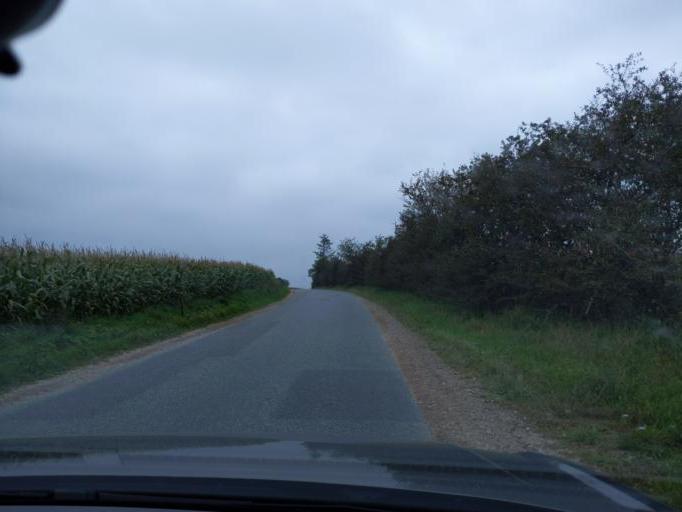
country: DK
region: Central Jutland
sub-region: Viborg Kommune
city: Stoholm
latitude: 56.5079
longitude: 9.2537
